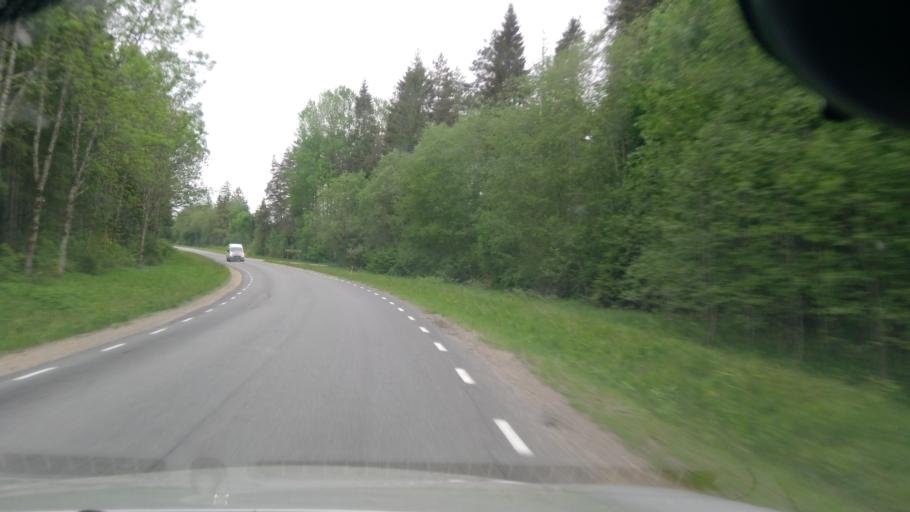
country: EE
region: Jaervamaa
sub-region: Koeru vald
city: Koeru
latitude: 58.9879
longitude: 26.0515
